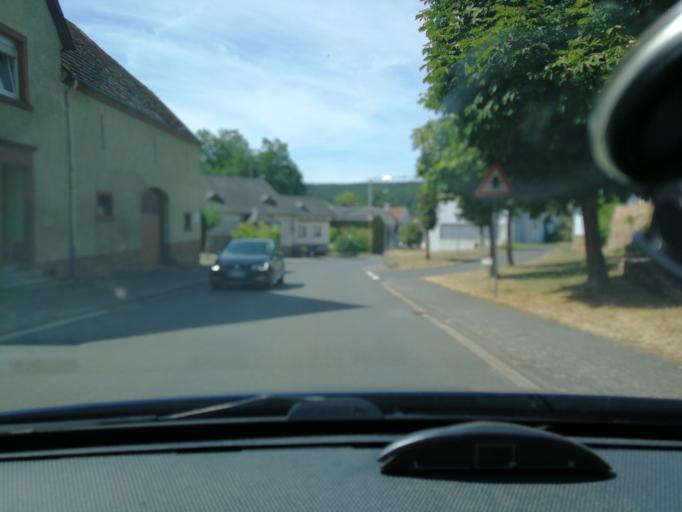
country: DE
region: Rheinland-Pfalz
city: Niersbach
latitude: 49.9385
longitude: 6.7447
